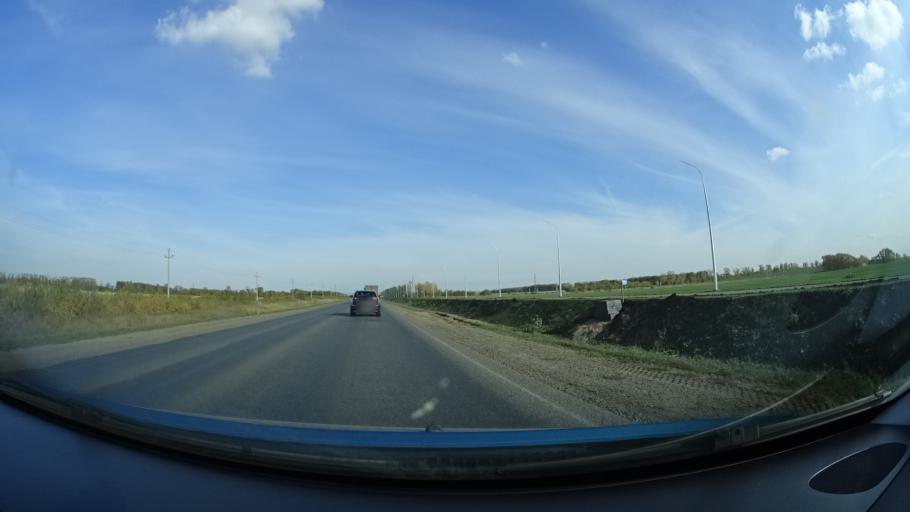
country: RU
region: Bashkortostan
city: Buzdyak
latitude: 54.6407
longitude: 54.5051
